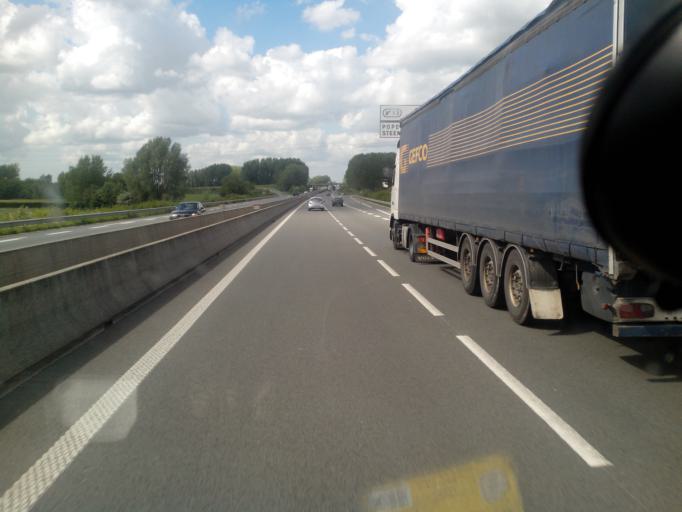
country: FR
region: Nord-Pas-de-Calais
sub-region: Departement du Nord
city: Steenvoorde
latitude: 50.8040
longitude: 2.6024
